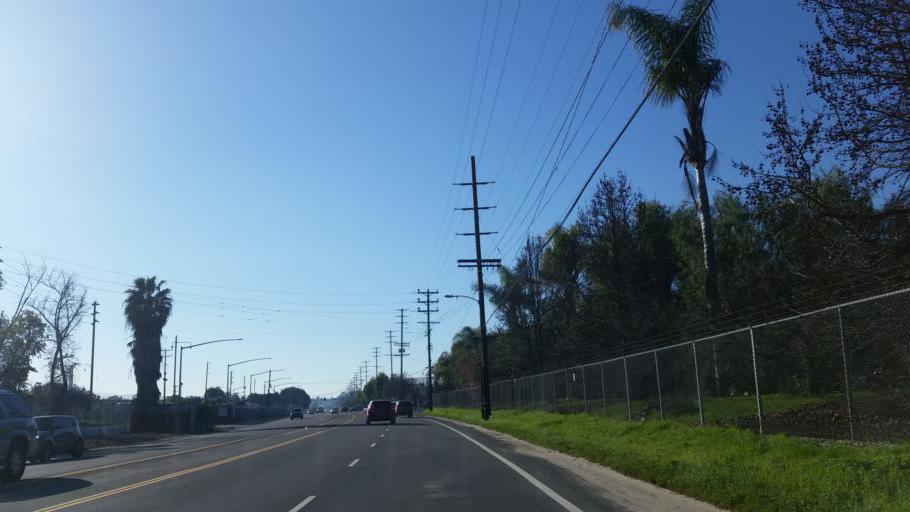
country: US
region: California
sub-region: Los Angeles County
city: San Pedro
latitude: 33.7676
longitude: -118.2940
